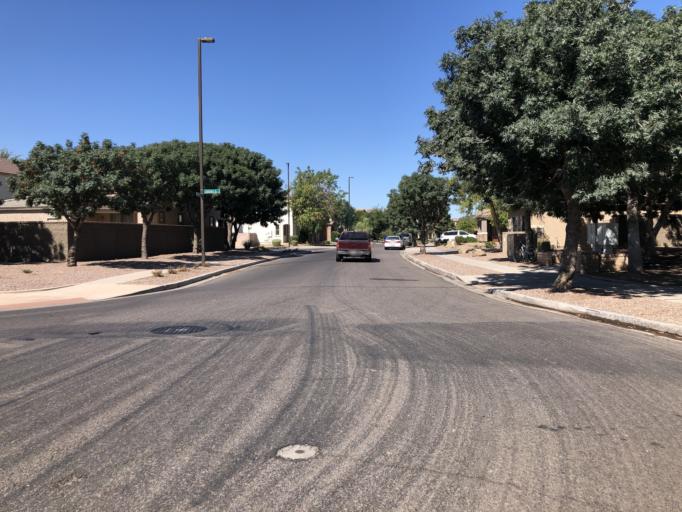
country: US
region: Arizona
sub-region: Maricopa County
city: Queen Creek
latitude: 33.2813
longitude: -111.6980
